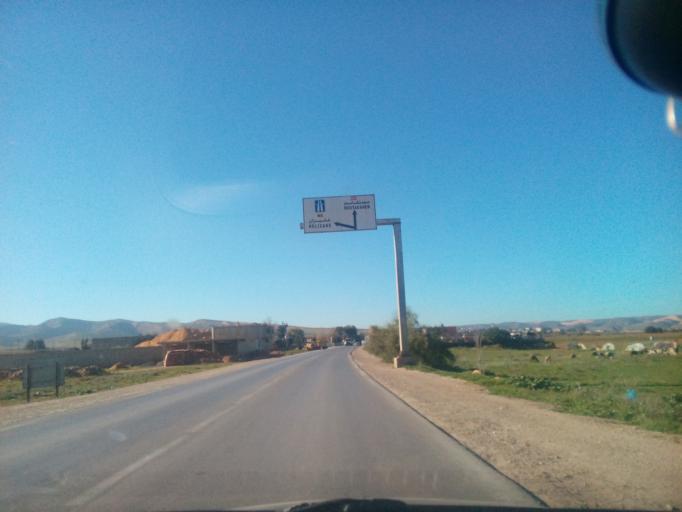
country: DZ
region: Relizane
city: Relizane
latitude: 35.8998
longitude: 0.5326
